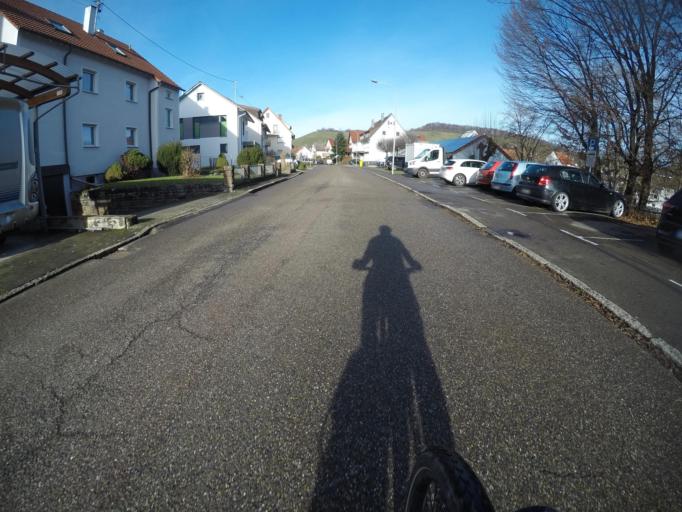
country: DE
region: Baden-Wuerttemberg
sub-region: Regierungsbezirk Stuttgart
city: Korb
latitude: 48.8393
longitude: 9.3631
